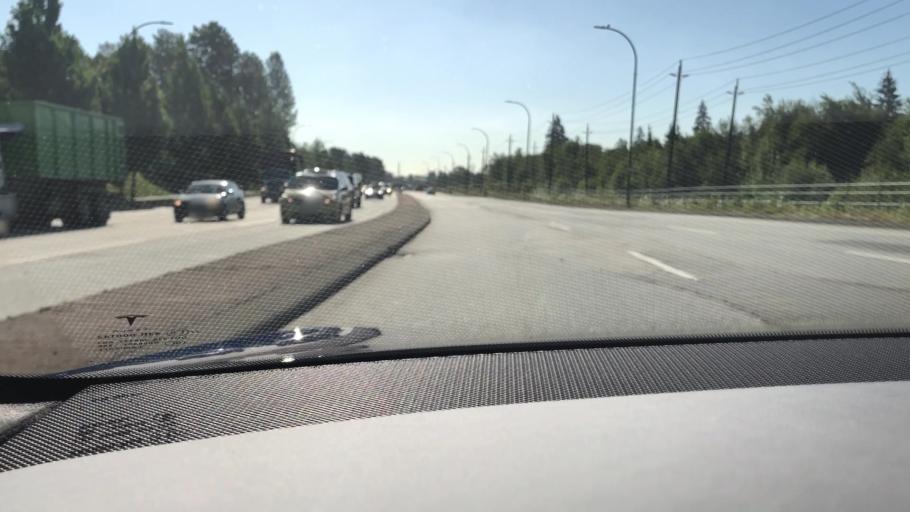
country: CA
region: British Columbia
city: New Westminster
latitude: 49.1975
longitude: -122.9755
